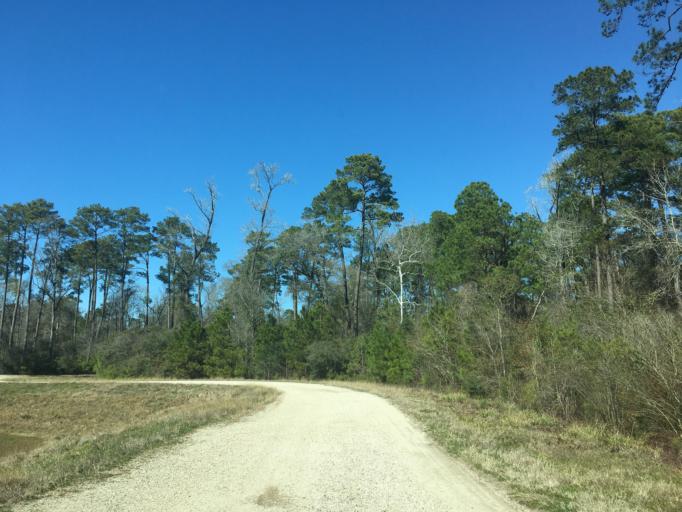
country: US
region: Texas
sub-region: Harris County
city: Spring
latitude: 30.1013
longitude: -95.4554
